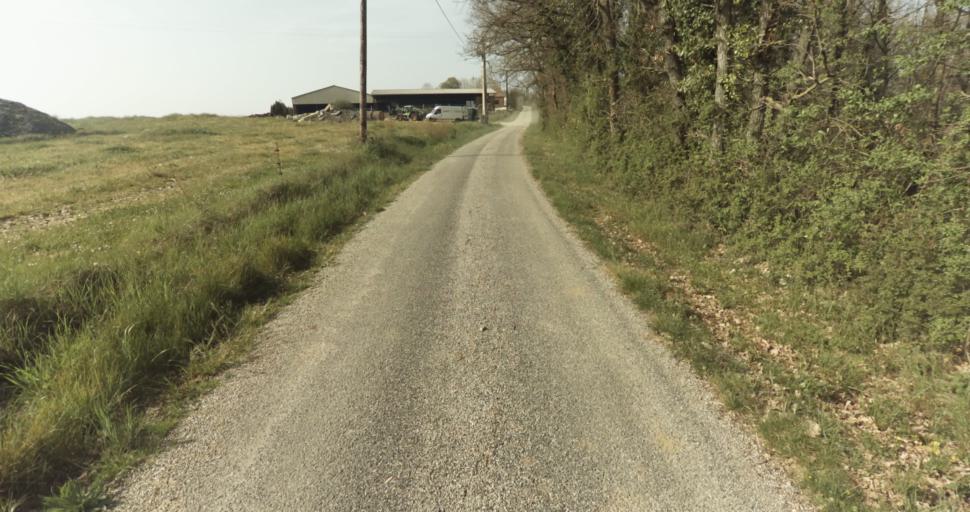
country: FR
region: Midi-Pyrenees
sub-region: Departement du Tarn-et-Garonne
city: Lafrancaise
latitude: 44.1554
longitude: 1.1717
